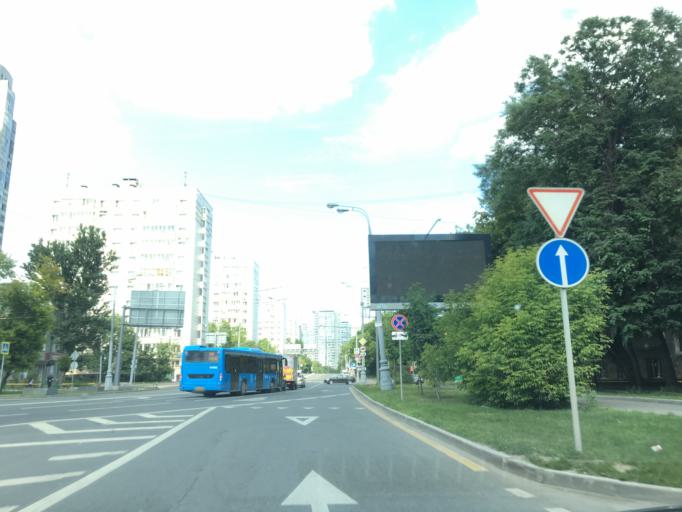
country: RU
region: Moskovskaya
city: Presnenskiy
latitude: 55.7551
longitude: 37.5361
